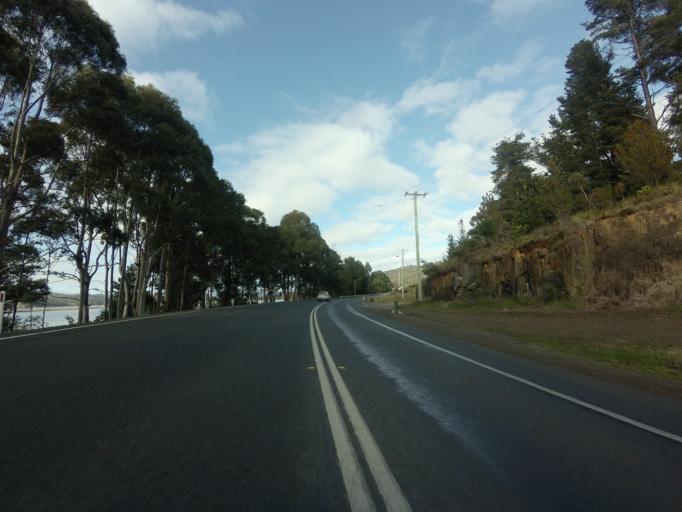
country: AU
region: Tasmania
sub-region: Huon Valley
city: Franklin
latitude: -43.1095
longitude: 147.0003
